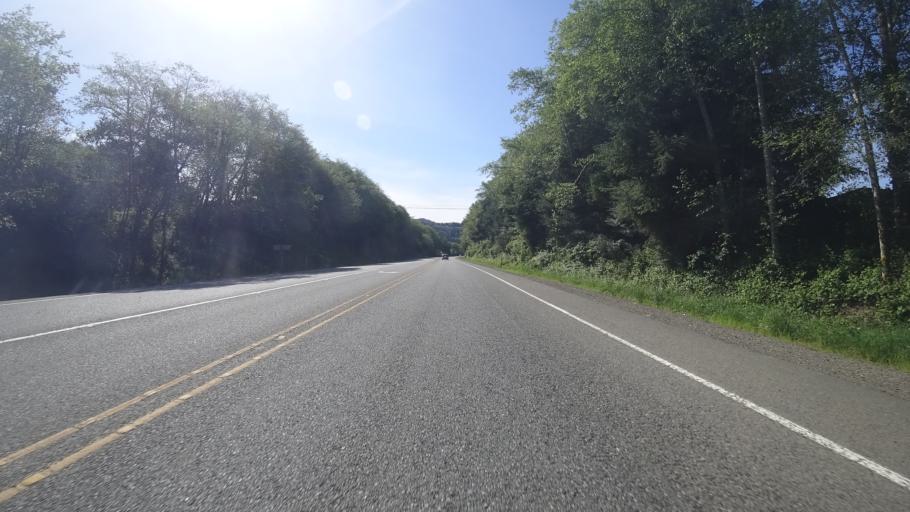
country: US
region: Oregon
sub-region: Curry County
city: Harbor
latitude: 42.0102
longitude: -124.2139
